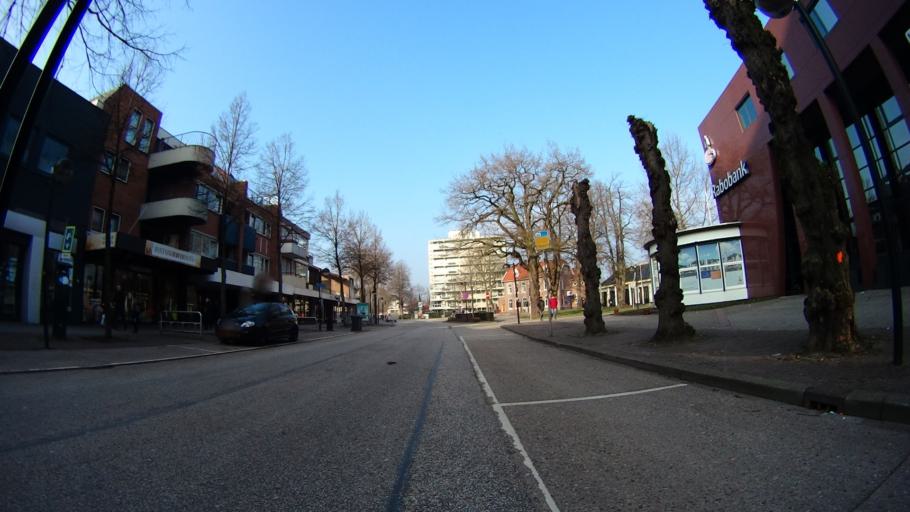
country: NL
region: Drenthe
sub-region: Gemeente Emmen
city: Emmen
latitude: 52.7833
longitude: 6.8967
